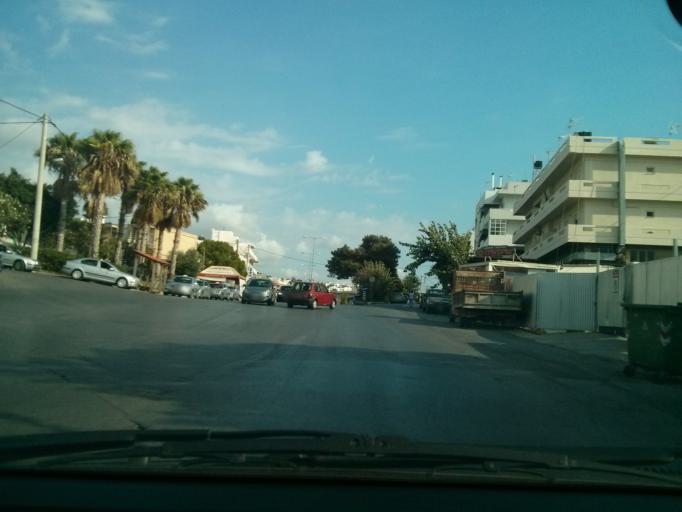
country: GR
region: Crete
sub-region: Nomos Irakleiou
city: Irakleion
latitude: 35.3237
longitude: 25.1406
